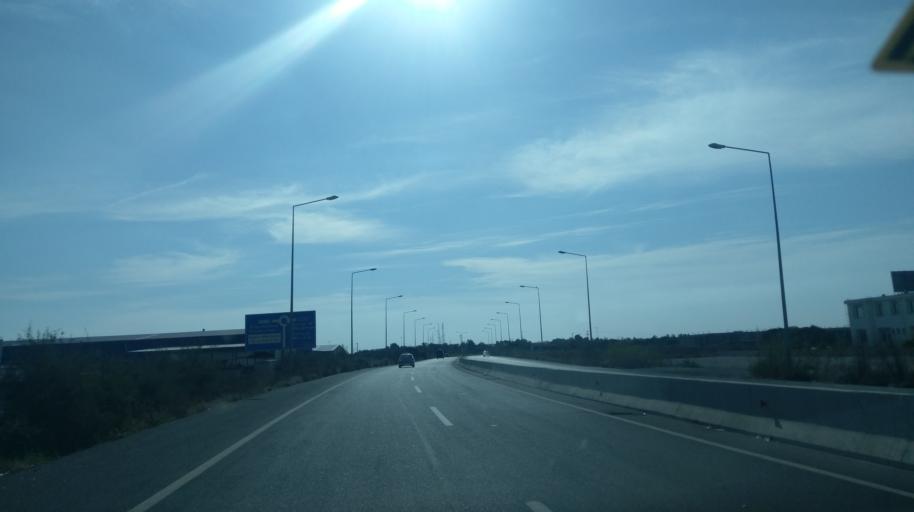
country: CY
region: Ammochostos
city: Famagusta
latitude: 35.1473
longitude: 33.8970
